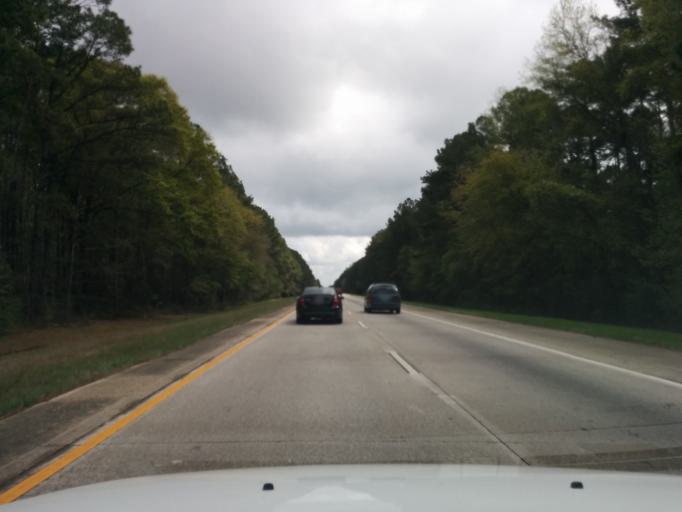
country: US
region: Georgia
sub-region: Evans County
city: Claxton
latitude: 32.3008
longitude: -81.8383
